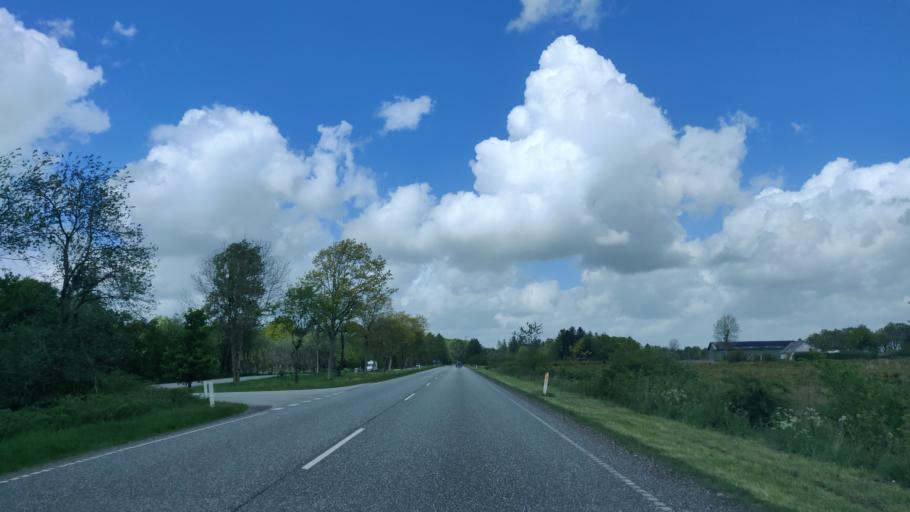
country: DK
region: Central Jutland
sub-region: Ikast-Brande Kommune
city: Bording Kirkeby
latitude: 56.2555
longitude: 9.3186
